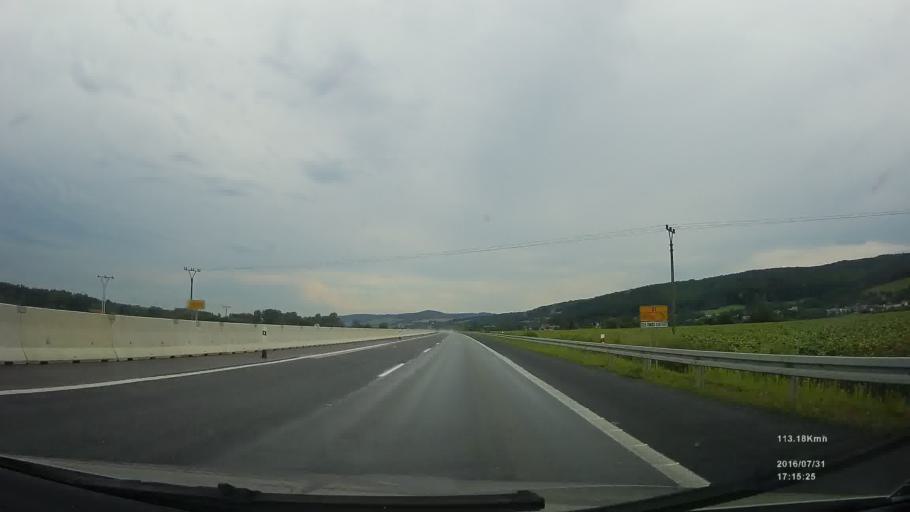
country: SK
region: Presovsky
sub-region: Okres Presov
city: Presov
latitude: 48.9087
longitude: 21.2501
